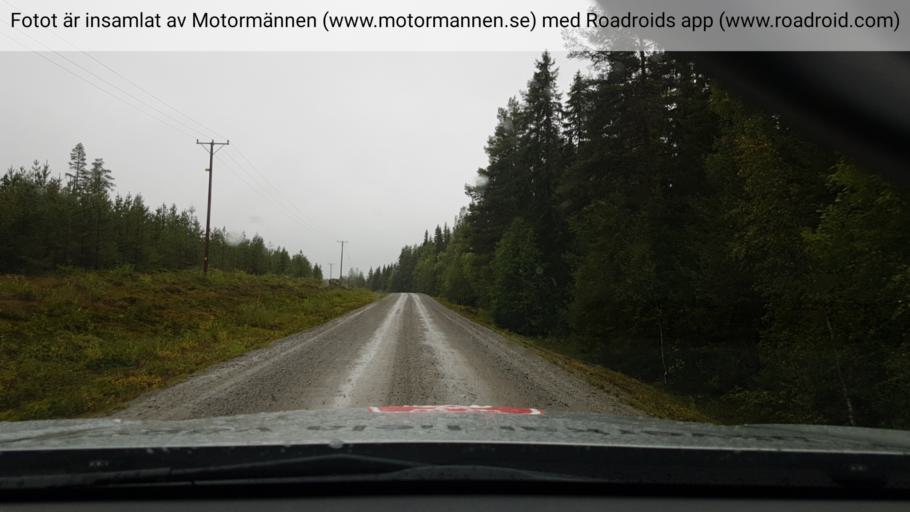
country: SE
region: Vaesterbotten
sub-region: Asele Kommun
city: Insjon
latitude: 64.0881
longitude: 17.8584
